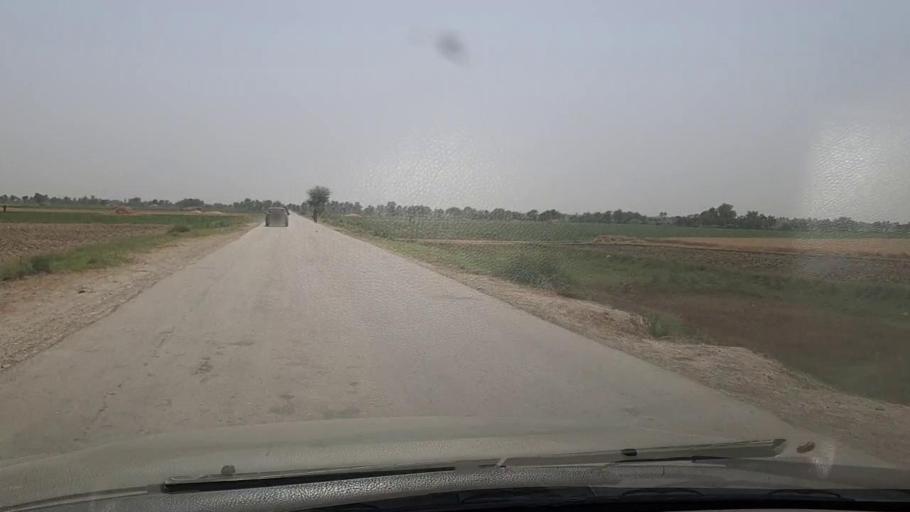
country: PK
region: Sindh
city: Kambar
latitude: 27.6264
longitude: 68.0256
